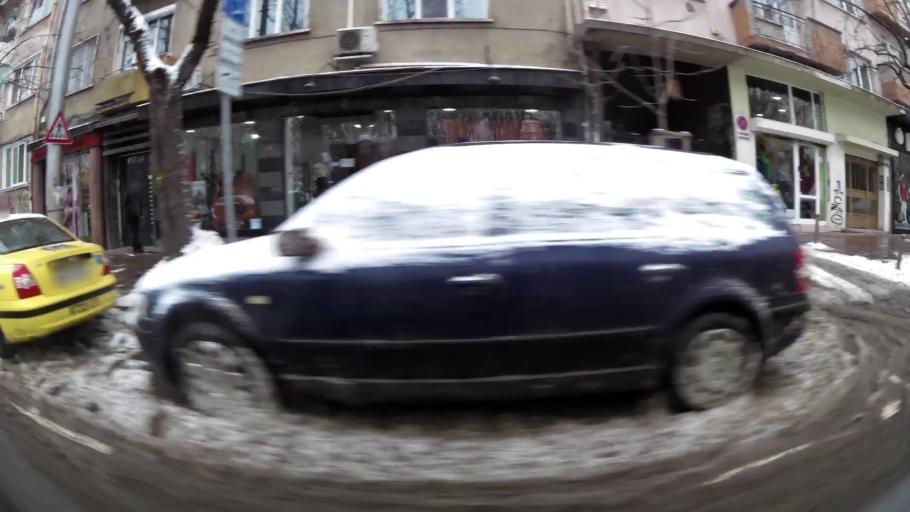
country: BG
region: Sofia-Capital
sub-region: Stolichna Obshtina
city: Sofia
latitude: 42.6961
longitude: 23.3415
